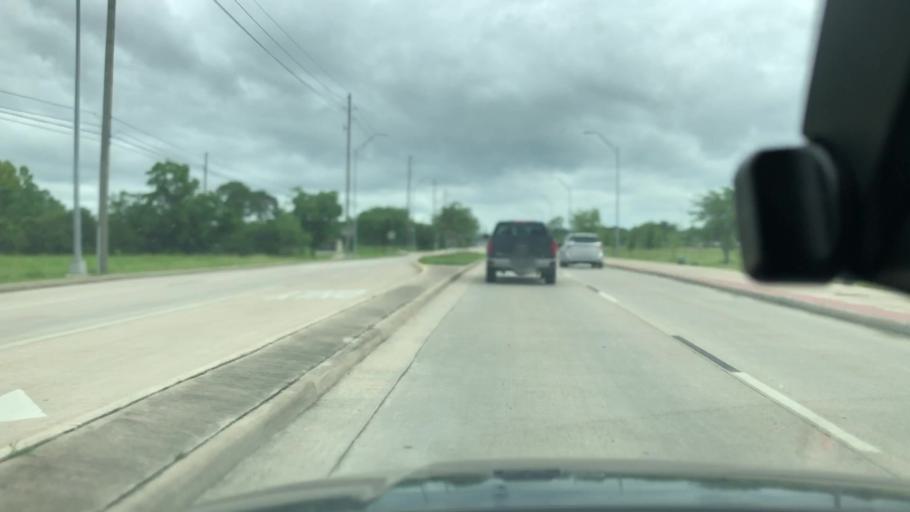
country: US
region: Texas
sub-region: Brazoria County
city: Brookside Village
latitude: 29.5757
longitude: -95.3509
